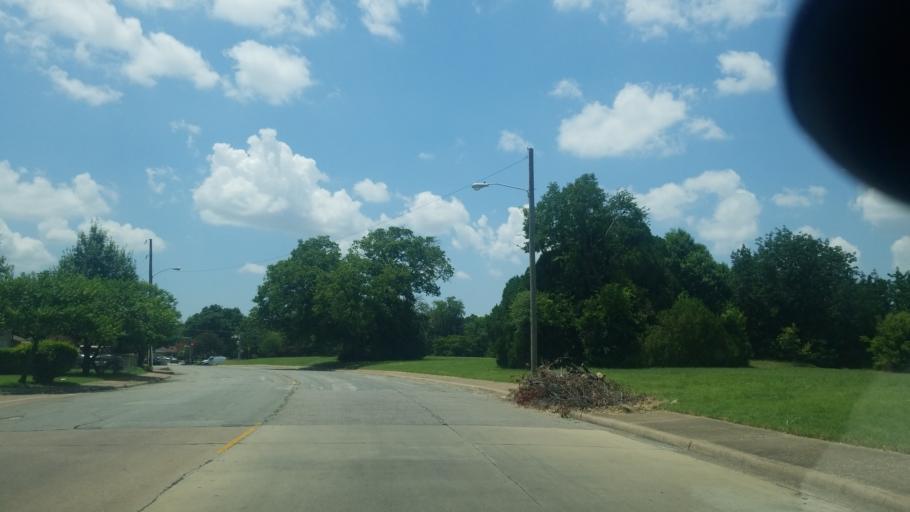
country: US
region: Texas
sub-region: Dallas County
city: Dallas
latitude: 32.7204
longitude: -96.7820
